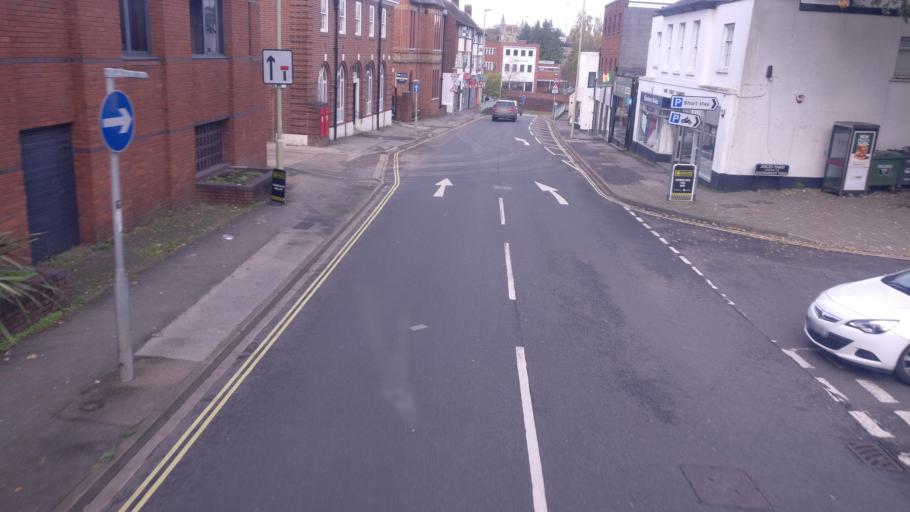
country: GB
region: England
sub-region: Hampshire
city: Basingstoke
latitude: 51.2627
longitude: -1.0889
